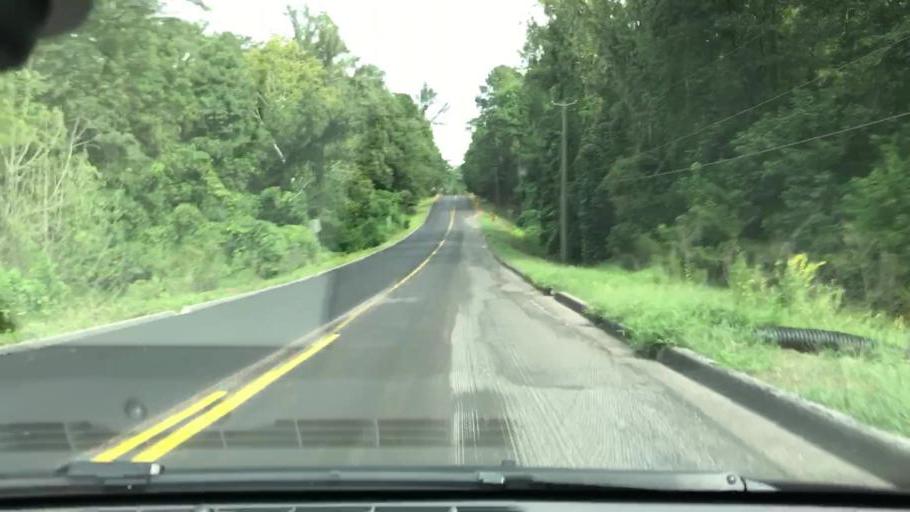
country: US
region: Georgia
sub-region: Clay County
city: Fort Gaines
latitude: 31.5959
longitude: -85.0432
